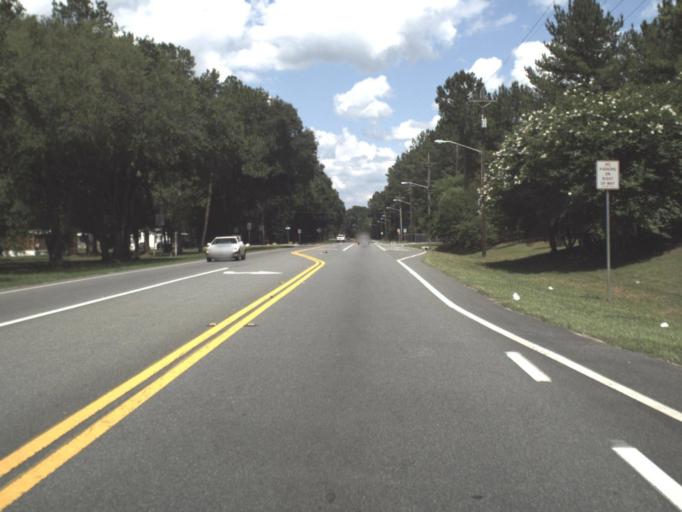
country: US
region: Florida
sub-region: Alachua County
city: Gainesville
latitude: 29.6736
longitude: -82.2635
